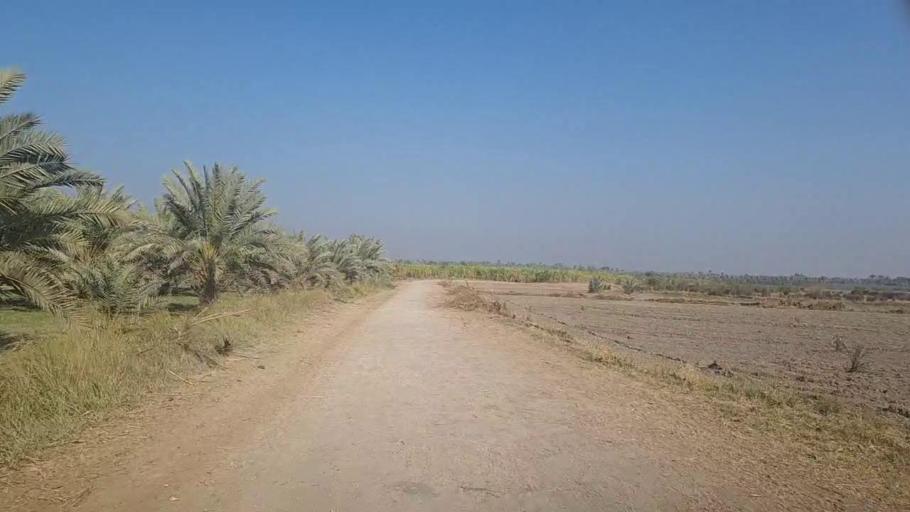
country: PK
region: Sindh
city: Khairpur
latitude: 27.4353
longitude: 68.7387
